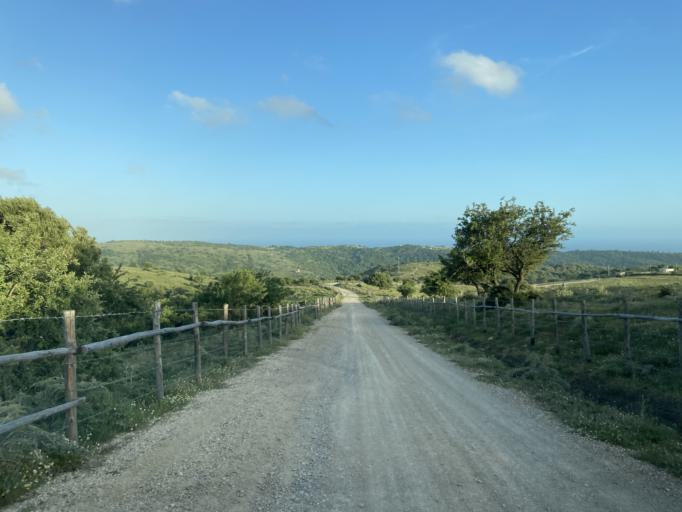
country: IT
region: Latium
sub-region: Citta metropolitana di Roma Capitale
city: Santa Marinella
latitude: 42.0870
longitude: 11.8518
